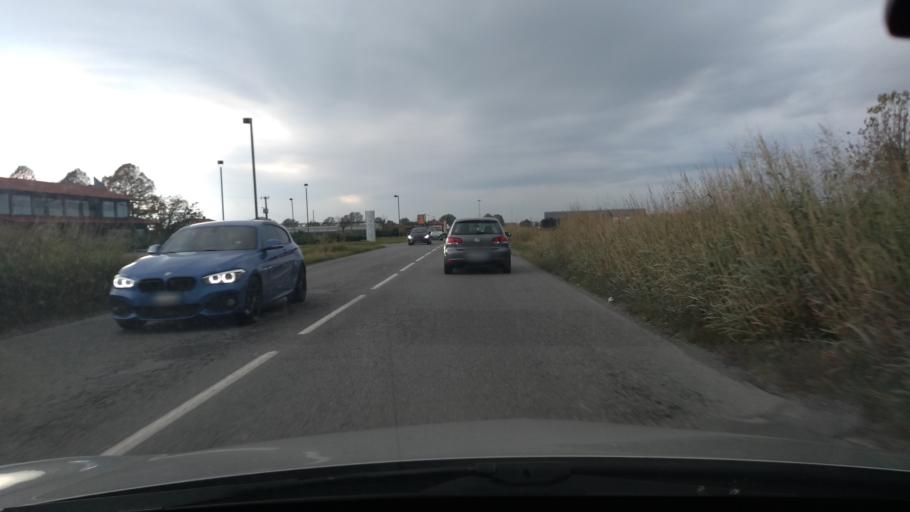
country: IT
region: Lombardy
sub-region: Provincia di Bergamo
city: Pognano
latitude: 45.5915
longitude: 9.6332
